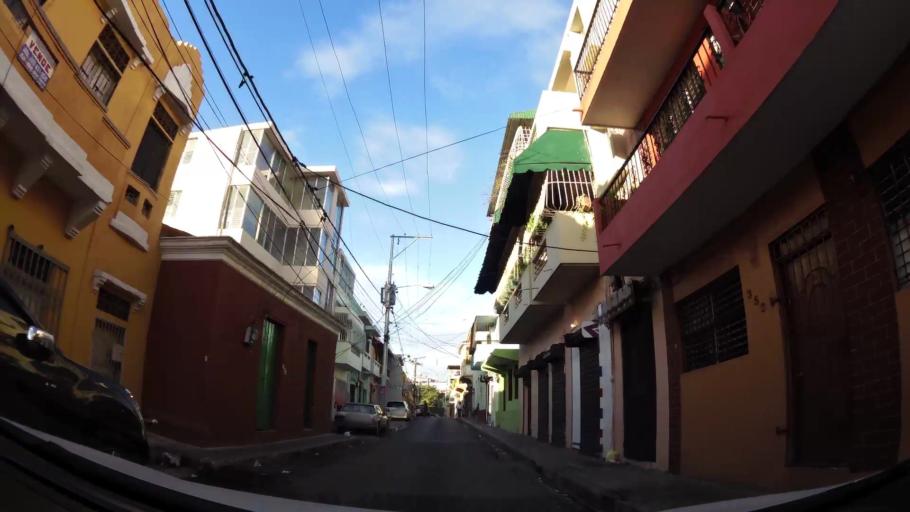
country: DO
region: Nacional
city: Ciudad Nueva
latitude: 18.4731
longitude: -69.8899
